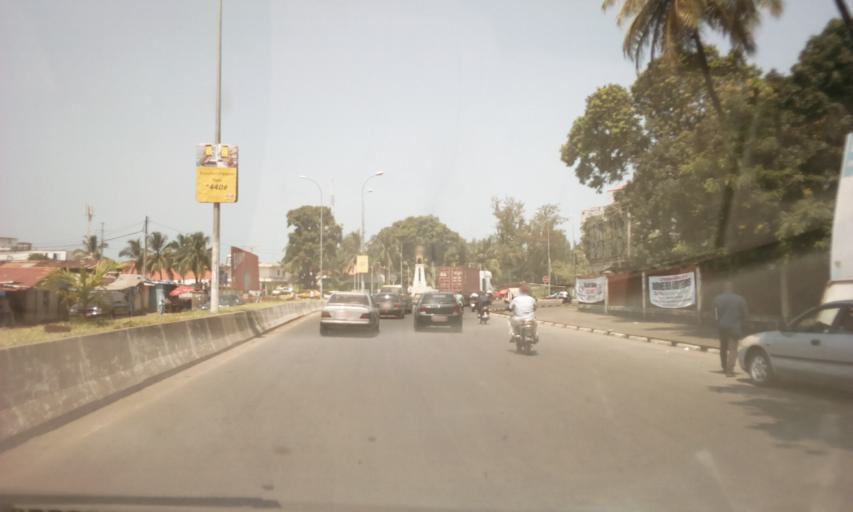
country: GN
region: Conakry
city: Camayenne
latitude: 9.5194
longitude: -13.6943
